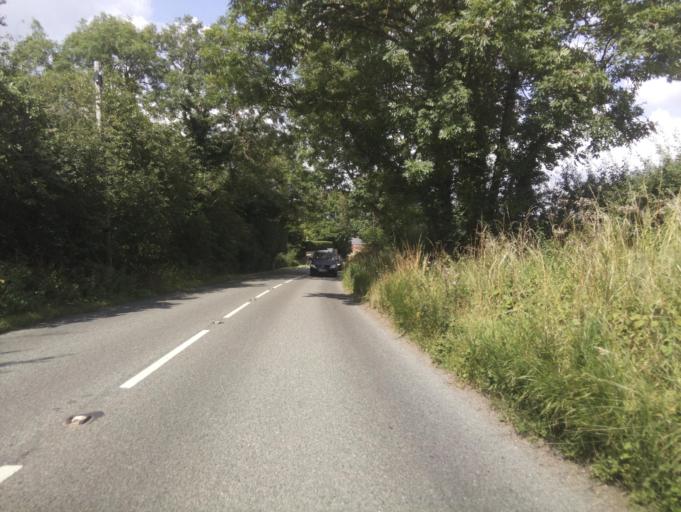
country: GB
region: England
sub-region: Wiltshire
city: Malmesbury
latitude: 51.5733
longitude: -2.0777
